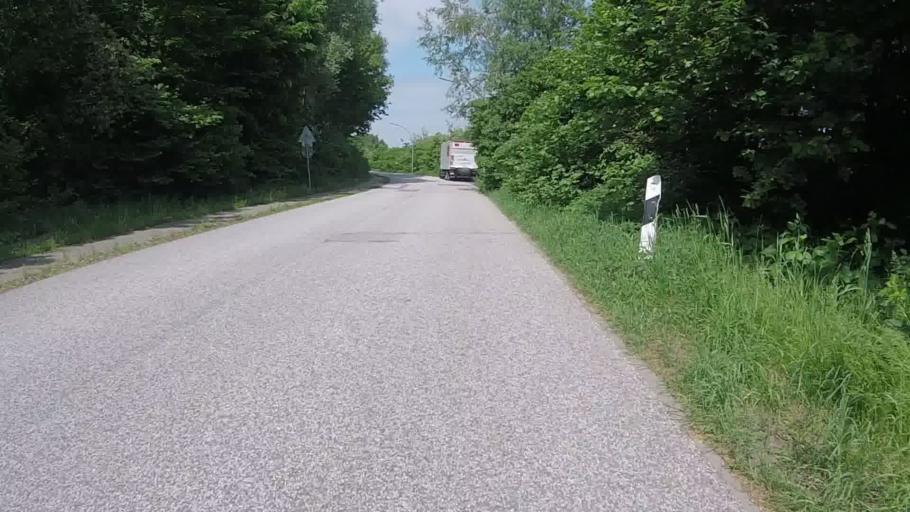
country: DE
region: Hamburg
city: Wandsbek
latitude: 53.5131
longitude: 10.1044
